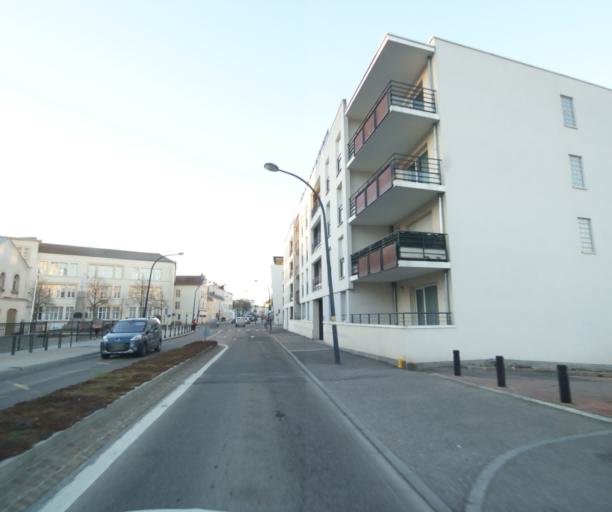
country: FR
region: Lorraine
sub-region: Departement de Meurthe-et-Moselle
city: Jarville-la-Malgrange
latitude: 48.6688
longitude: 6.2078
